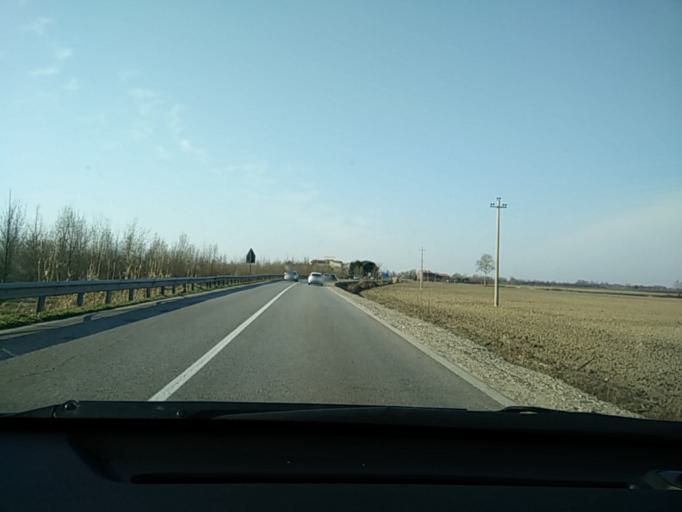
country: IT
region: Veneto
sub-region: Provincia di Venezia
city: Quarto d'Altino
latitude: 45.5365
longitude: 12.3981
